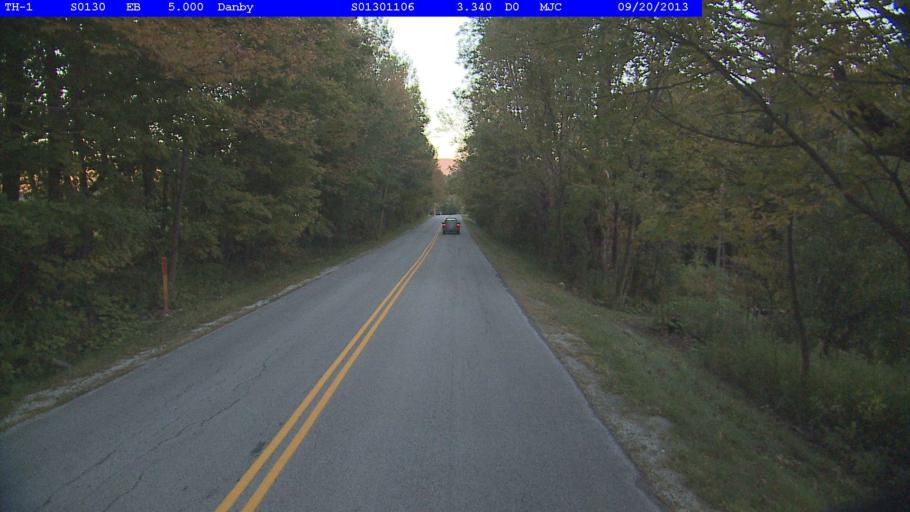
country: US
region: Vermont
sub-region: Bennington County
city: Manchester Center
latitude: 43.3573
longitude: -73.0643
